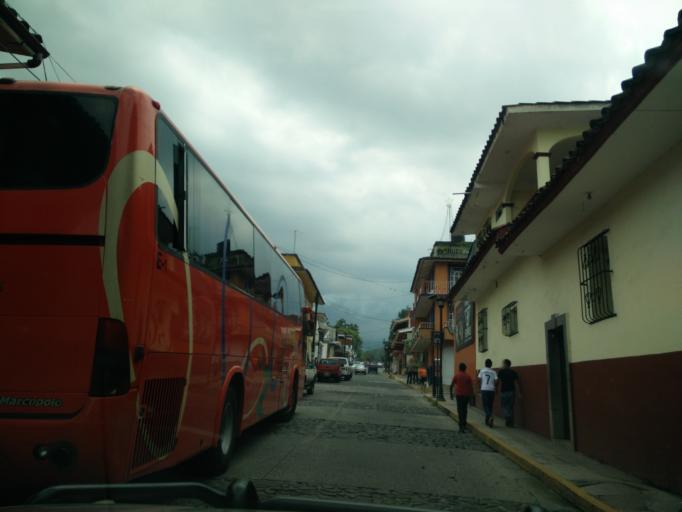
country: MX
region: Veracruz
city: Xico
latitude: 19.4229
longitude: -97.0094
